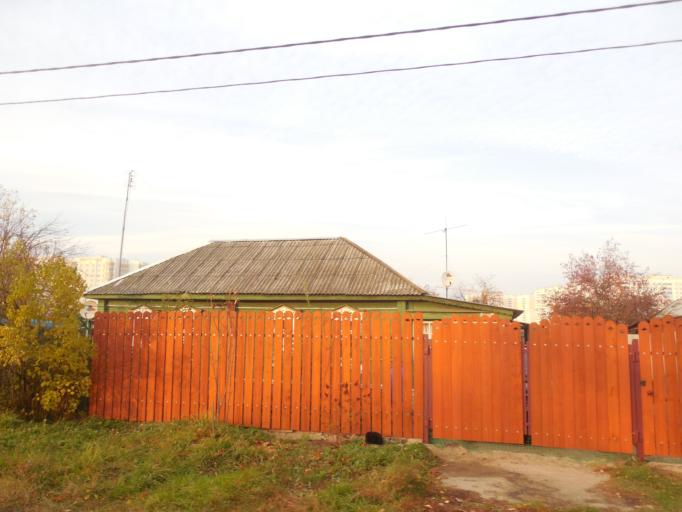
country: RU
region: Moskovskaya
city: Shcherbinka
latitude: 55.4988
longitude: 37.5814
